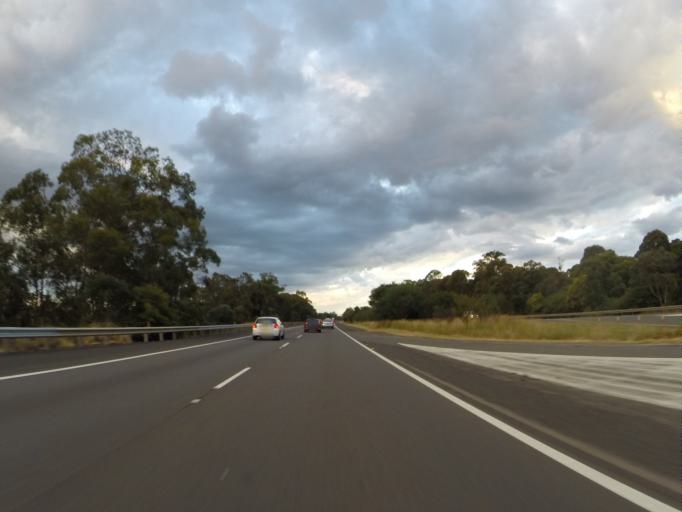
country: AU
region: New South Wales
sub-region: Wollondilly
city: Douglas Park
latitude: -34.1885
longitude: 150.7152
